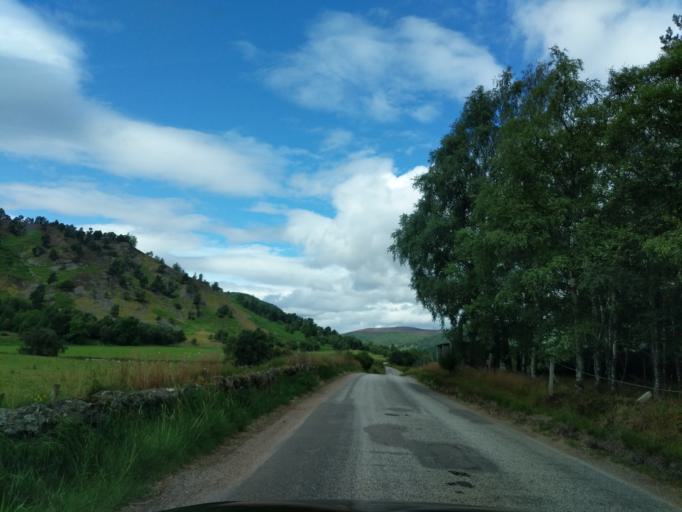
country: GB
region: Scotland
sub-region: Aberdeenshire
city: Ballater
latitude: 57.0460
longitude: -3.0947
